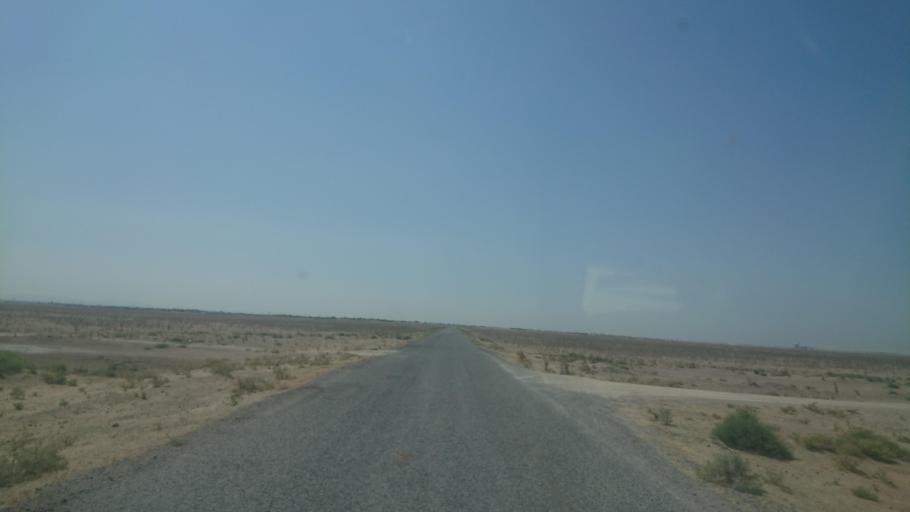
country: TR
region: Aksaray
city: Yesilova
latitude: 38.3118
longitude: 33.7379
